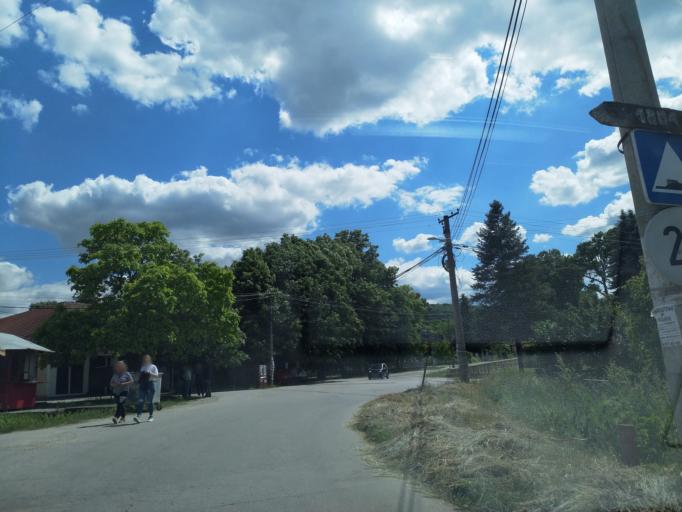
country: RS
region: Central Serbia
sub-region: Pomoravski Okrug
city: Jagodina
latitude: 43.9459
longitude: 21.2963
